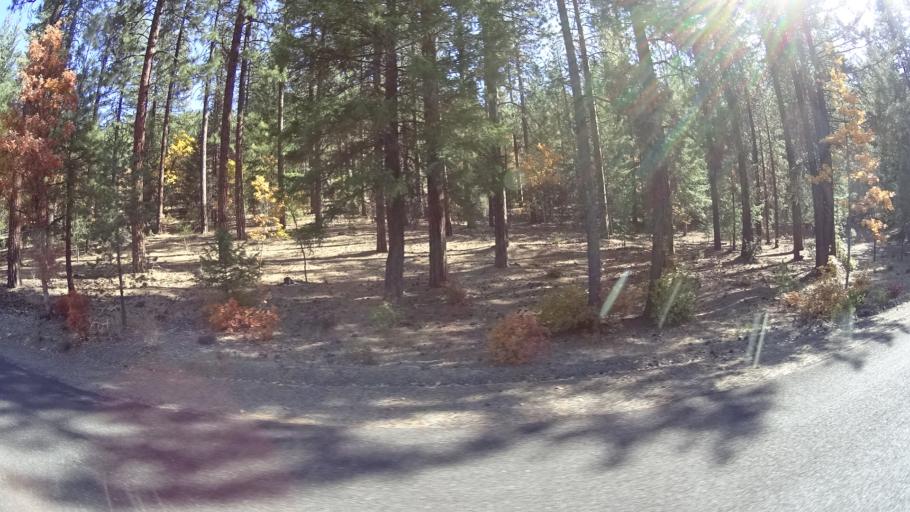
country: US
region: California
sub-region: Siskiyou County
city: Yreka
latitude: 41.6622
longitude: -122.8518
